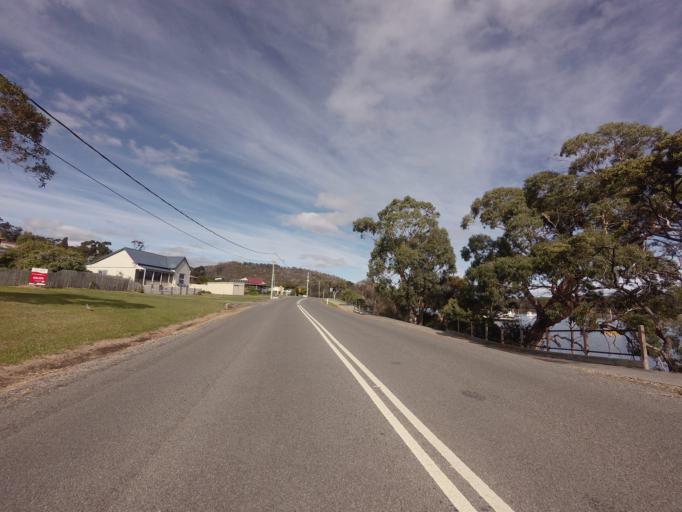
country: AU
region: Tasmania
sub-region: Clarence
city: Sandford
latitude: -43.1027
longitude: 147.7421
